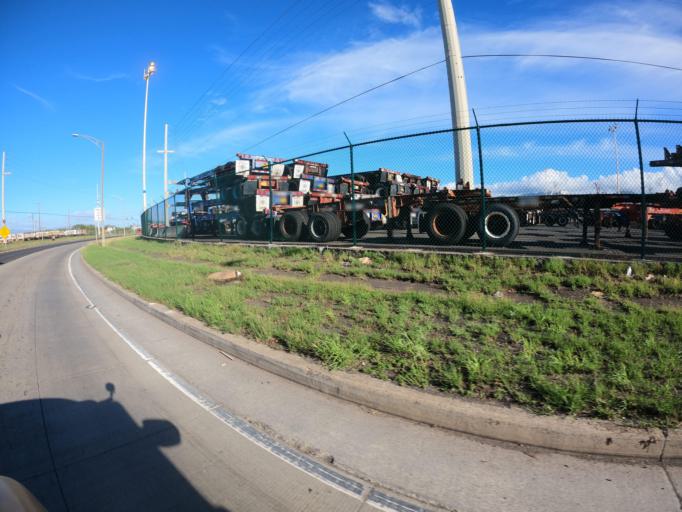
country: US
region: Hawaii
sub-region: Honolulu County
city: Honolulu
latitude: 21.3084
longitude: -157.8852
